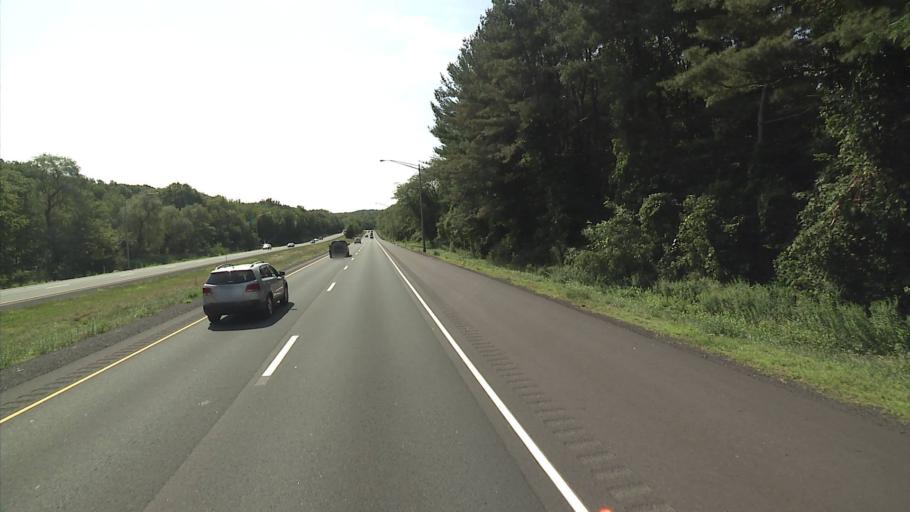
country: US
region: Connecticut
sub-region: Hartford County
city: Glastonbury Center
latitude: 41.6717
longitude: -72.5365
